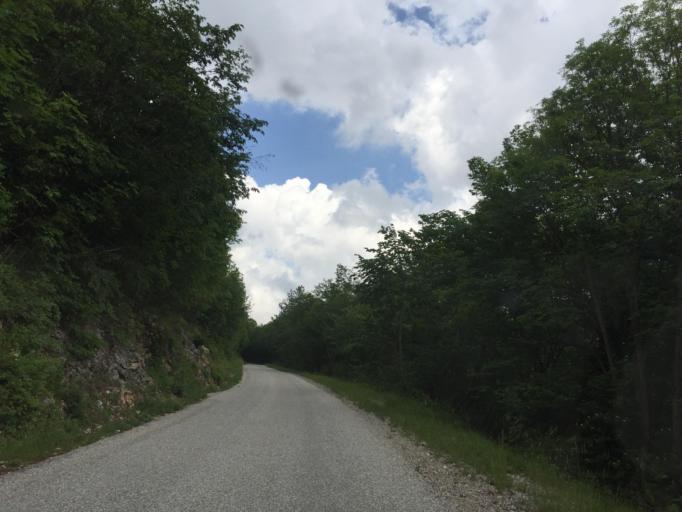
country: SI
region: Nova Gorica
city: Kromberk
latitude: 46.0110
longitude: 13.7259
